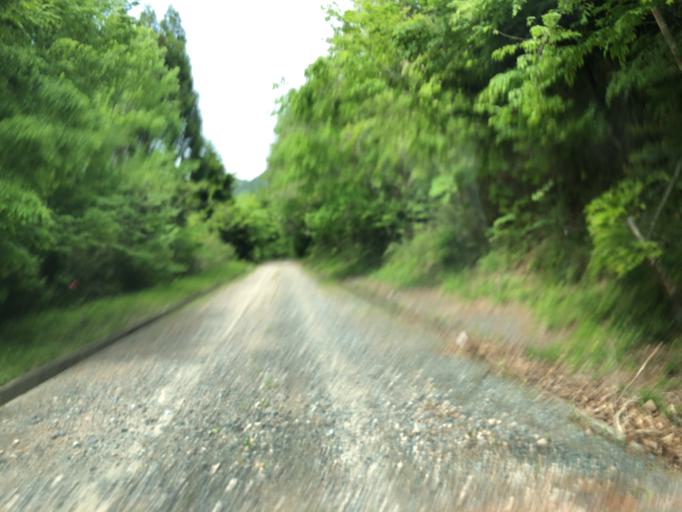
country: JP
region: Miyagi
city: Marumori
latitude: 37.7329
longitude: 140.8314
